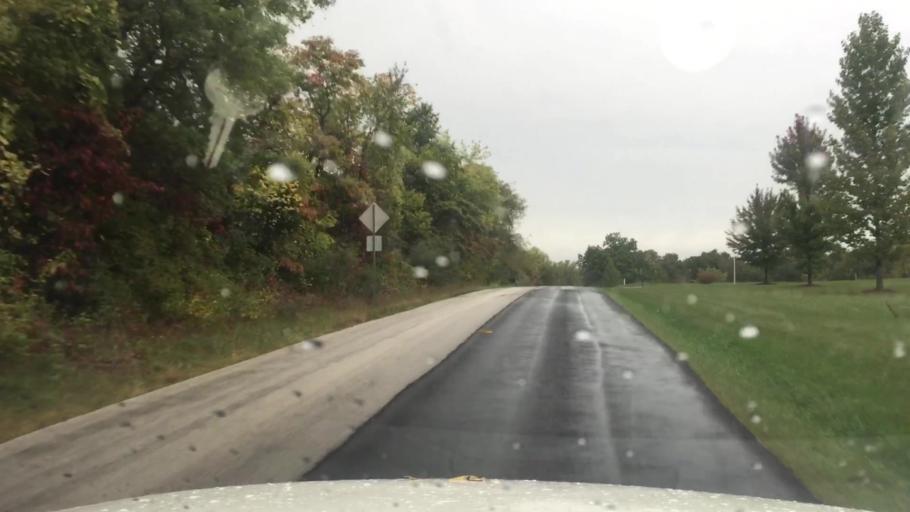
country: US
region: Missouri
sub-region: Boone County
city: Columbia
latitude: 38.9313
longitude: -92.4675
